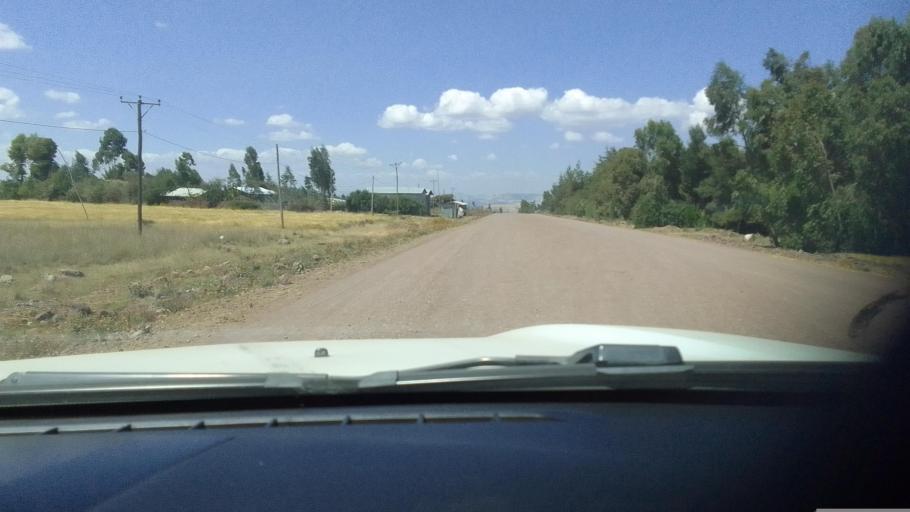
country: ET
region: Oromiya
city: Hagere Hiywet
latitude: 8.9191
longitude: 37.8674
